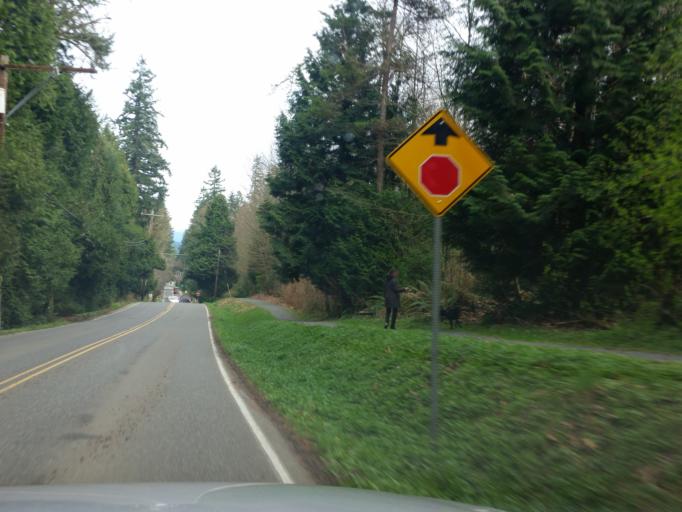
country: US
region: Washington
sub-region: King County
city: Woodinville
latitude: 47.7539
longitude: -122.1231
